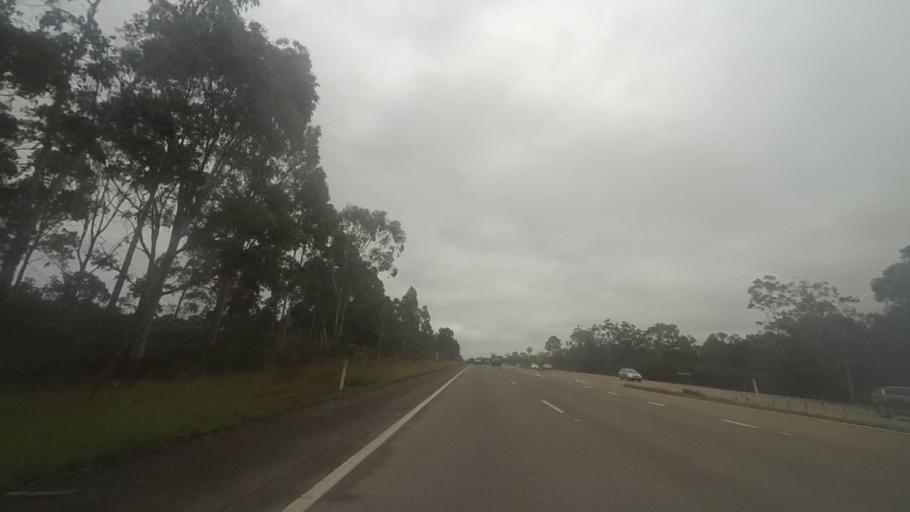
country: AU
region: New South Wales
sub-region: Port Stephens Shire
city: Medowie
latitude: -32.6820
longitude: 151.8153
